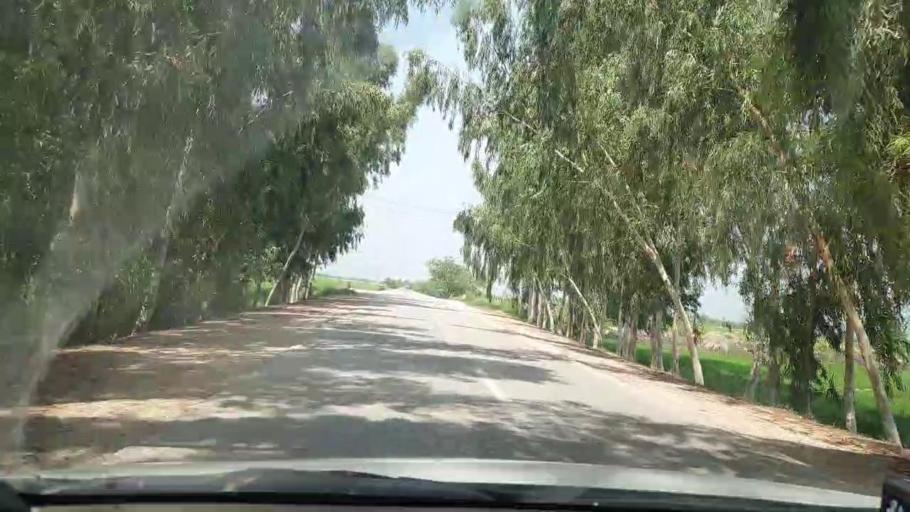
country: PK
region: Sindh
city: Rustam jo Goth
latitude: 27.9571
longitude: 68.7414
